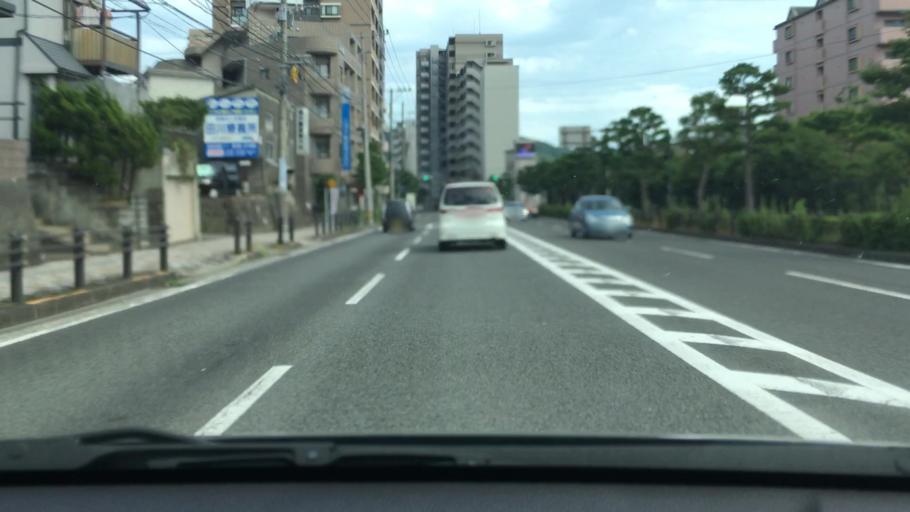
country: JP
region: Nagasaki
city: Obita
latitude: 32.7960
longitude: 129.8553
